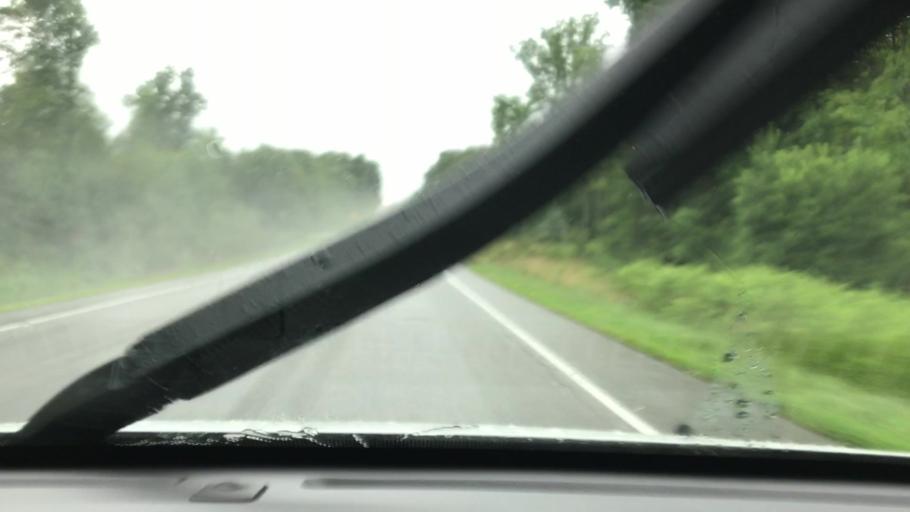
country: US
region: Pennsylvania
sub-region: Centre County
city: Philipsburg
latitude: 40.8466
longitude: -78.2205
